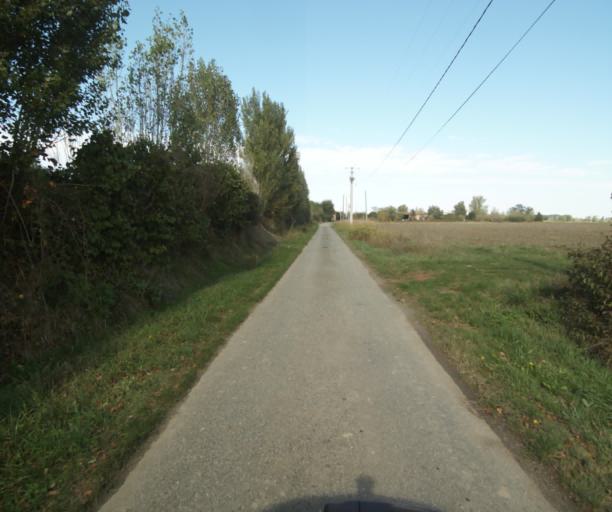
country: FR
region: Midi-Pyrenees
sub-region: Departement du Tarn-et-Garonne
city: Verdun-sur-Garonne
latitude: 43.8815
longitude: 1.2230
